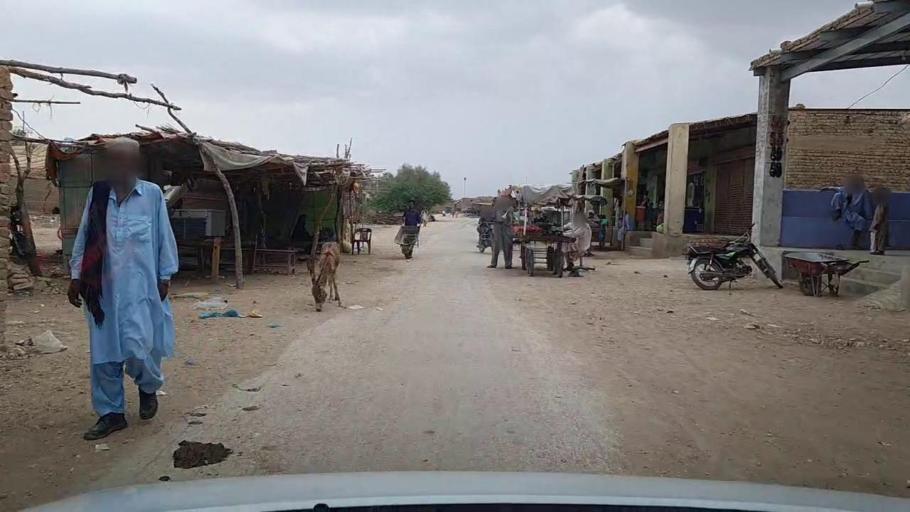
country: PK
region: Sindh
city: Sehwan
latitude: 26.3402
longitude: 67.7214
